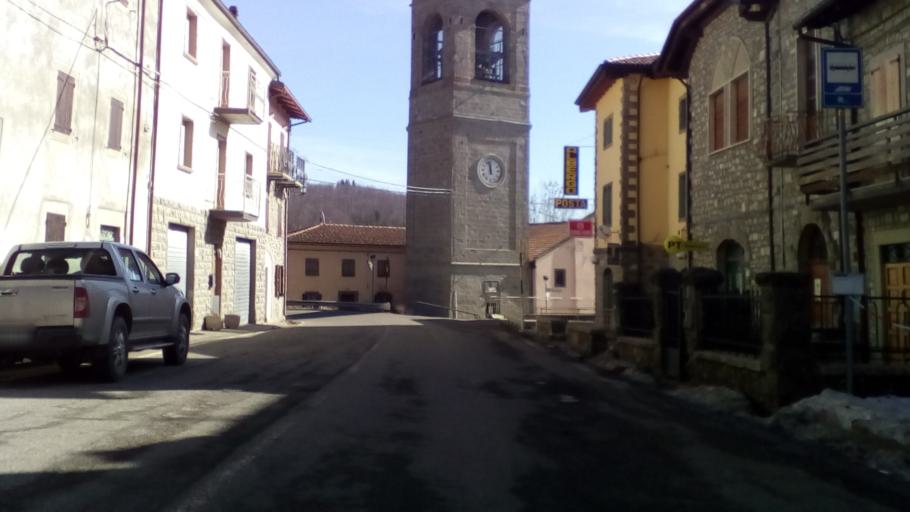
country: IT
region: Emilia-Romagna
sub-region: Provincia di Modena
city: Riolunato
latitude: 44.2655
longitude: 10.6505
